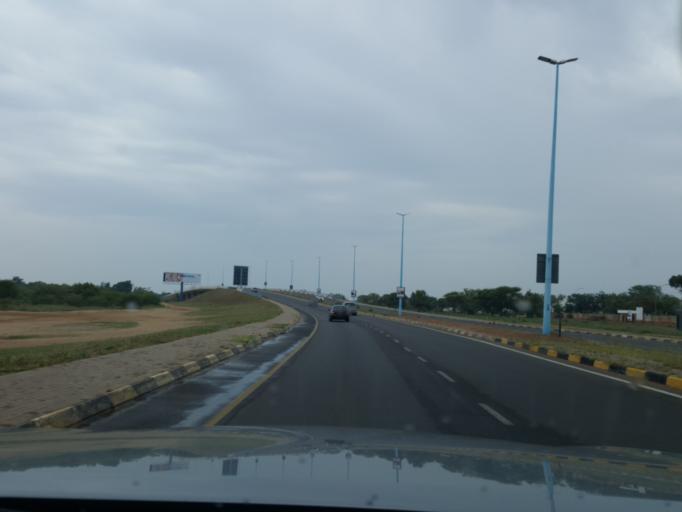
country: BW
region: South East
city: Gaborone
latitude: -24.6113
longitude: 25.9259
